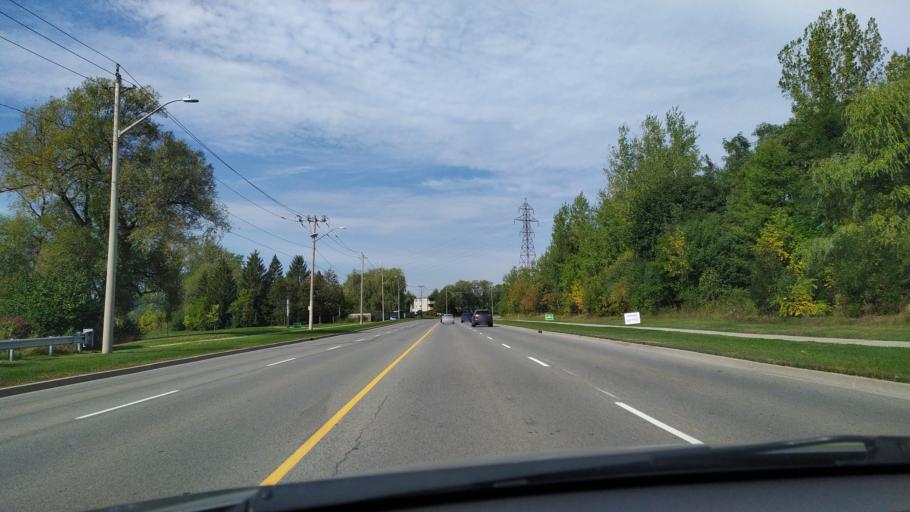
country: CA
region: Ontario
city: Kitchener
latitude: 43.4367
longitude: -80.5166
